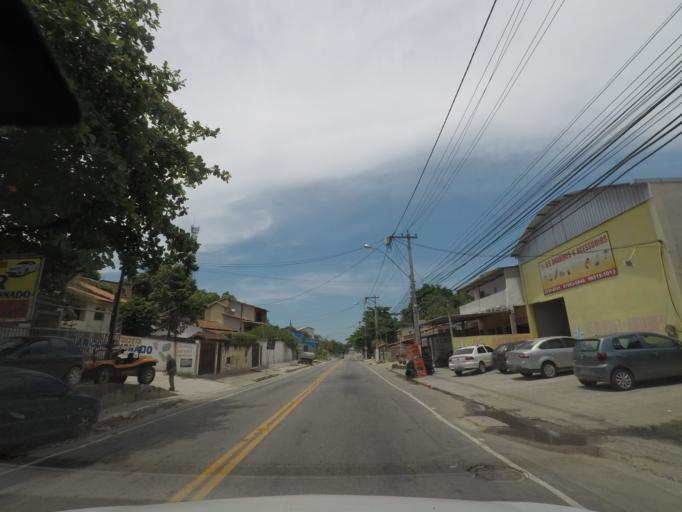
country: BR
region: Rio de Janeiro
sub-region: Marica
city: Marica
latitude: -22.9346
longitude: -42.8259
